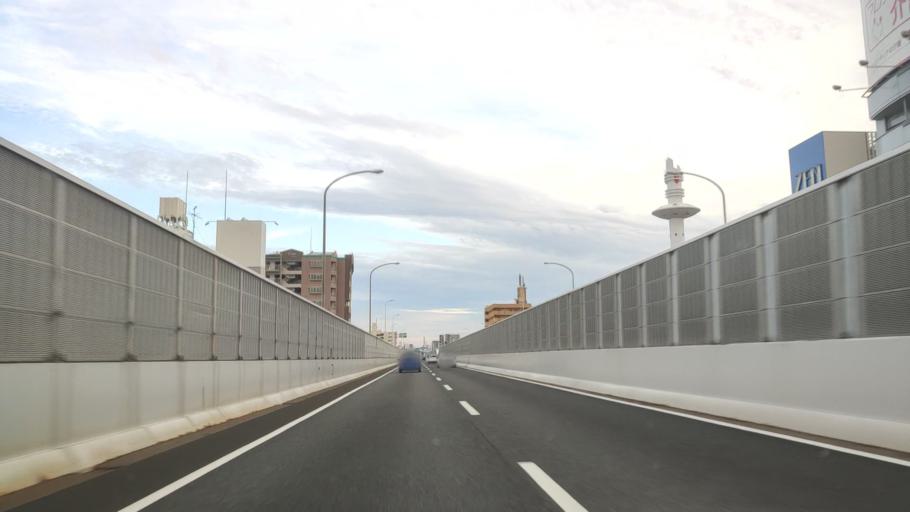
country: JP
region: Aichi
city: Nagoya-shi
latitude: 35.2095
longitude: 136.9111
